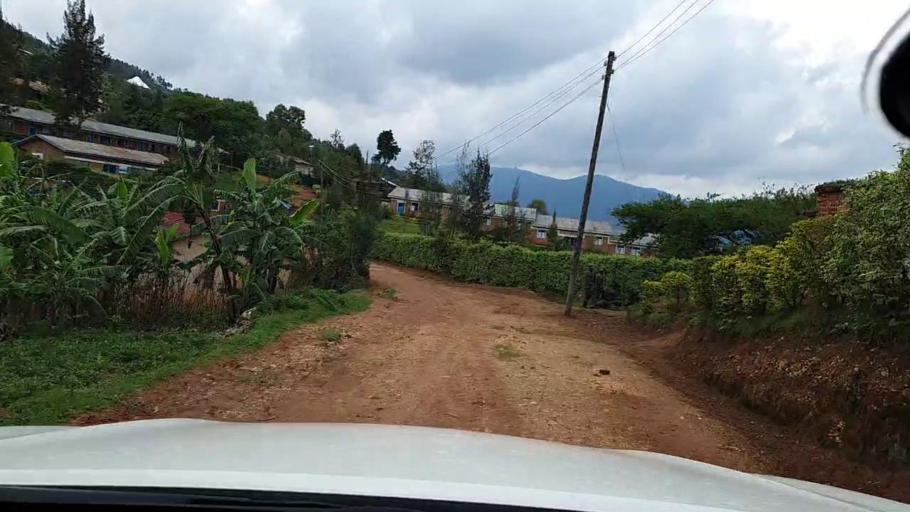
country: RW
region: Western Province
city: Kibuye
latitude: -2.1880
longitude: 29.2964
